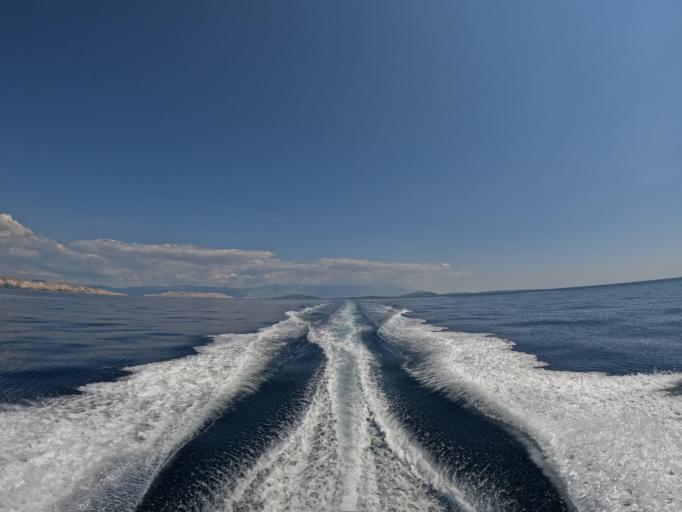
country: HR
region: Primorsko-Goranska
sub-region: Grad Krk
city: Krk
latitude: 44.9153
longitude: 14.5793
